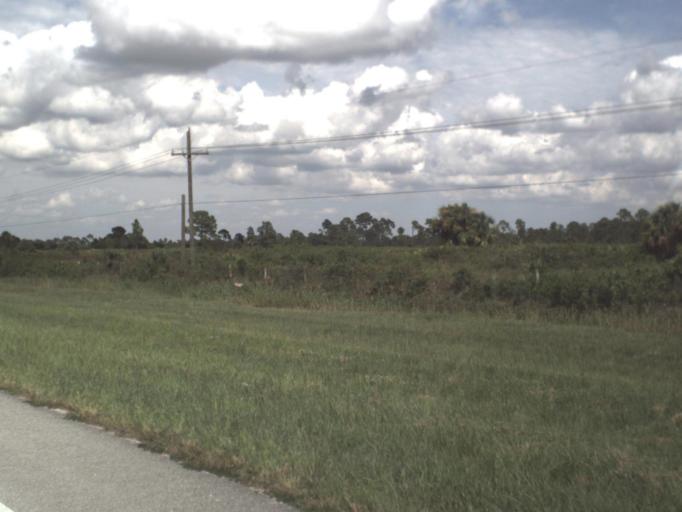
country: US
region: Florida
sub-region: Hendry County
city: Port LaBelle
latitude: 26.6095
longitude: -81.4366
